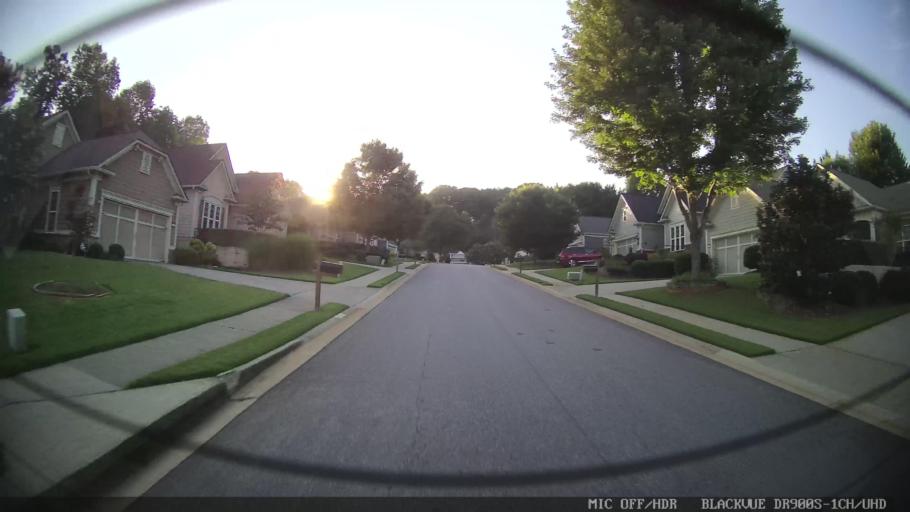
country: US
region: Georgia
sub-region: Forsyth County
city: Cumming
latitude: 34.2164
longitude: -84.2352
